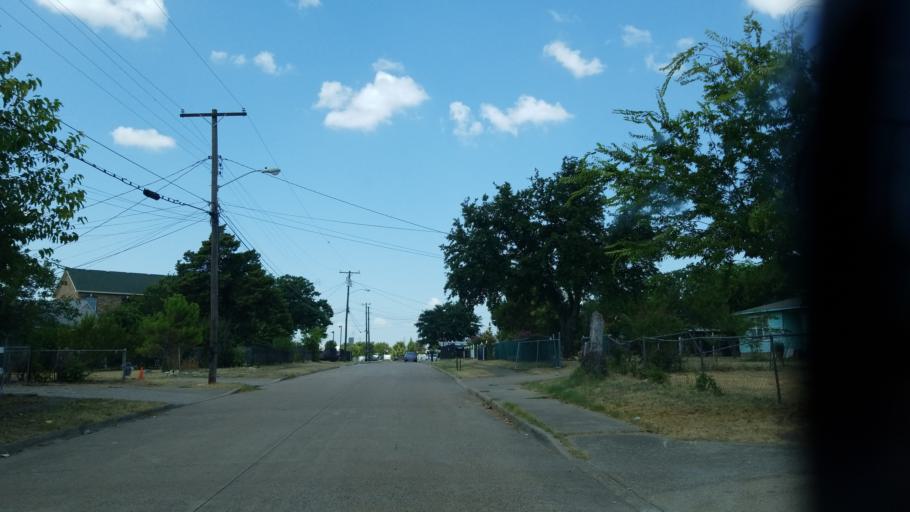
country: US
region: Texas
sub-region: Dallas County
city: Cockrell Hill
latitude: 32.7120
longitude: -96.9069
